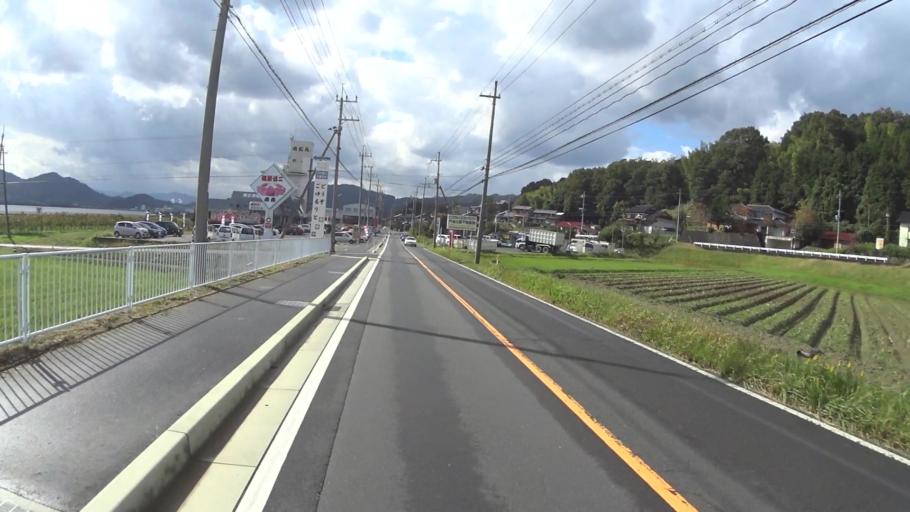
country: JP
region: Kyoto
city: Miyazu
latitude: 35.5757
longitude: 135.1763
